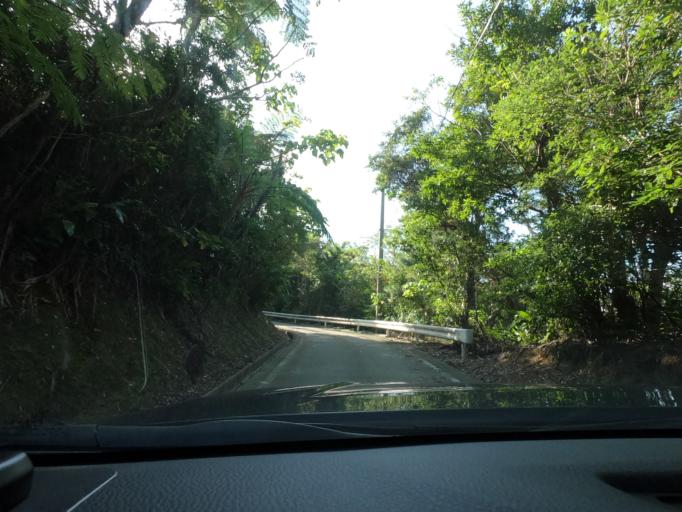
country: JP
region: Okinawa
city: Nago
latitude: 26.7558
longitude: 128.2003
